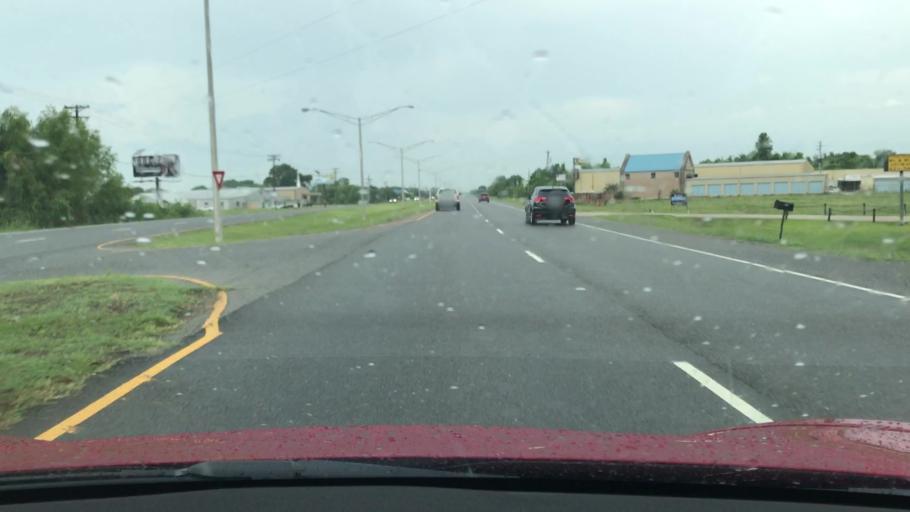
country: US
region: Louisiana
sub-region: Bossier Parish
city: Bossier City
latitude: 32.4031
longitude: -93.6952
